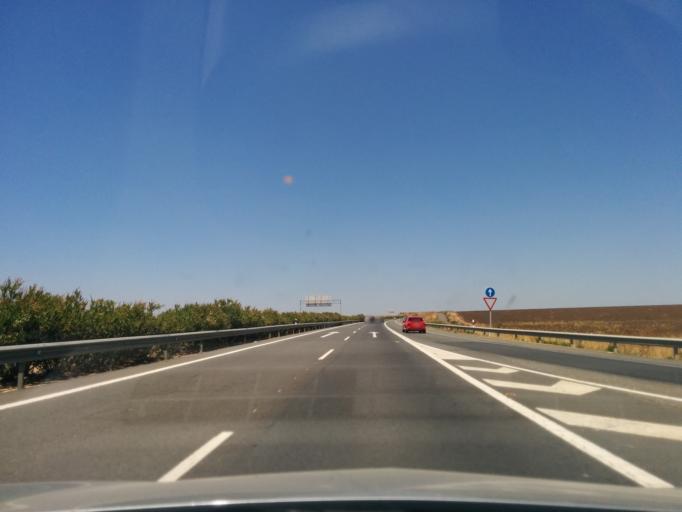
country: ES
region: Andalusia
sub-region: Provincia de Huelva
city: Huelva
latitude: 37.3245
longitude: -6.9101
